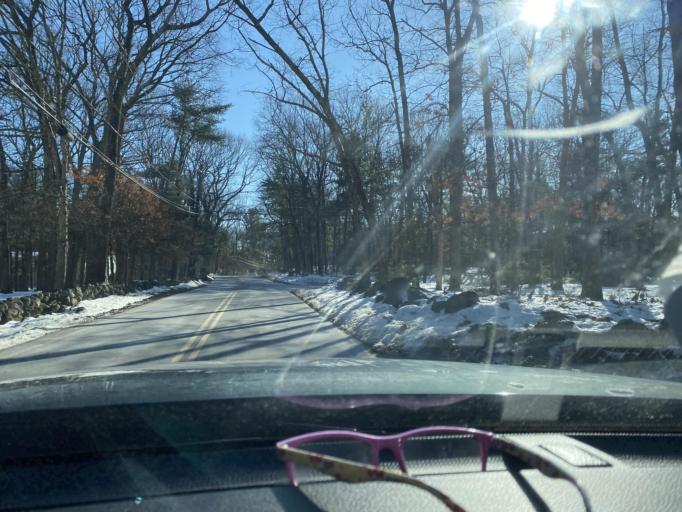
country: US
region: Massachusetts
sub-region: Norfolk County
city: Walpole
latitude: 42.1747
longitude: -71.2660
